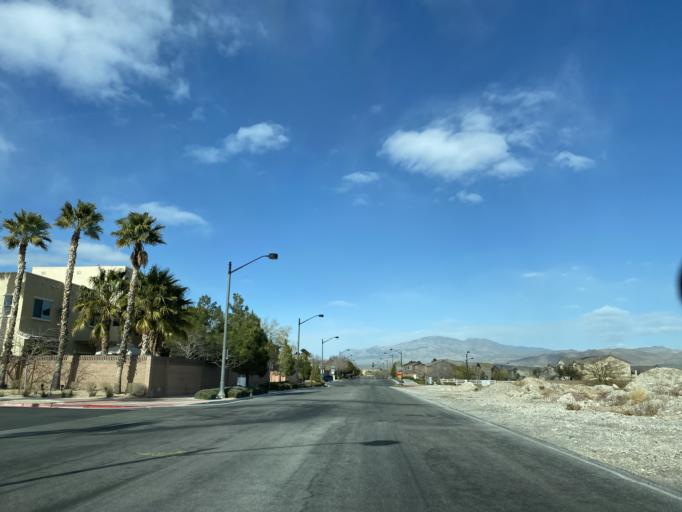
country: US
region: Nevada
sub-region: Clark County
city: Summerlin South
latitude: 36.3055
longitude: -115.3013
